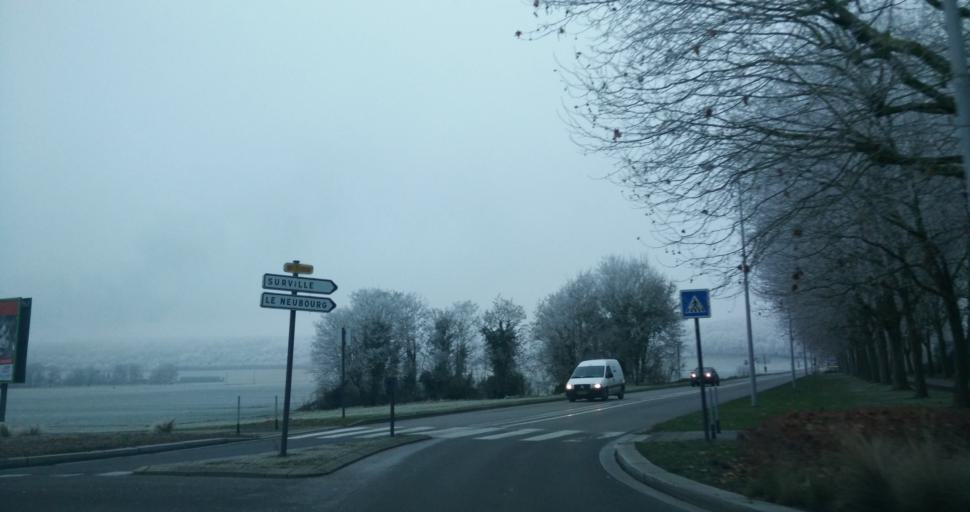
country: FR
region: Haute-Normandie
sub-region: Departement de l'Eure
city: Louviers
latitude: 49.2074
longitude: 1.1497
